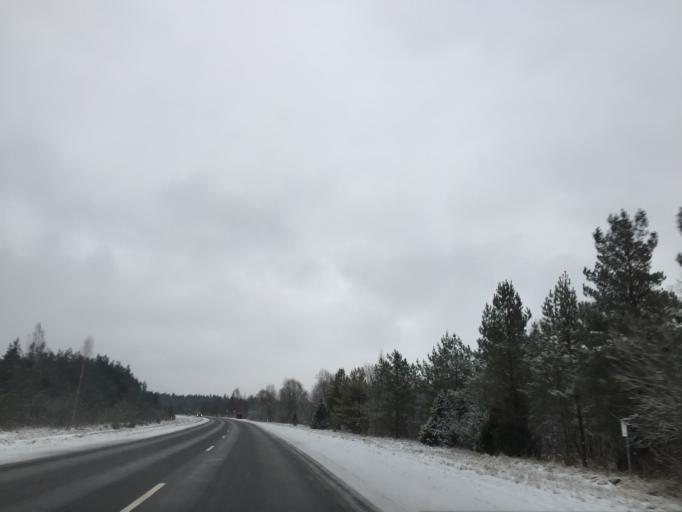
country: EE
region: Laeaene
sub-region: Lihula vald
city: Lihula
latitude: 58.6123
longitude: 23.9232
